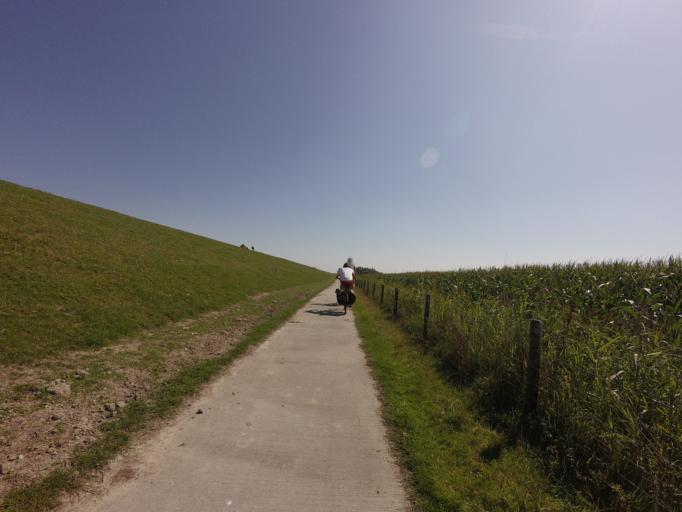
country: NL
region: Friesland
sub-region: Gemeente Dongeradeel
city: Anjum
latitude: 53.3996
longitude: 6.0995
